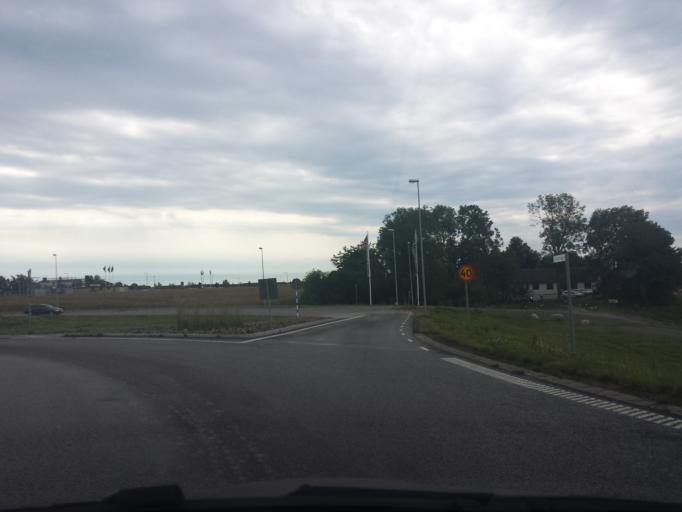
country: SE
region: Skane
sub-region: Ystads Kommun
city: Ystad
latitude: 55.4399
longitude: 13.7886
